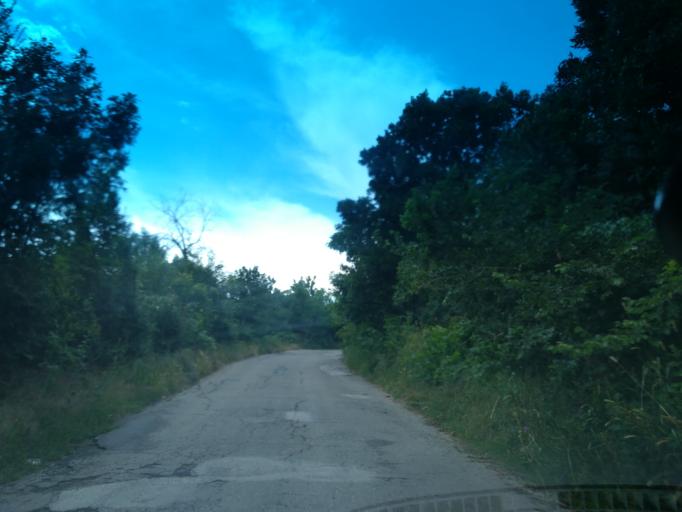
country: BG
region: Khaskovo
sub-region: Obshtina Mineralni Bani
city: Mineralni Bani
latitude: 41.9985
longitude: 25.2269
